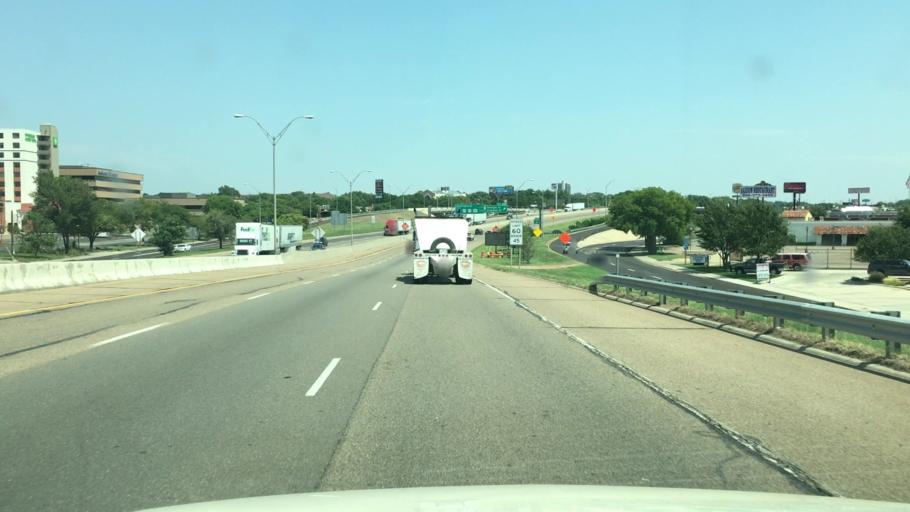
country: US
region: Texas
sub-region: Potter County
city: Amarillo
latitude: 35.1935
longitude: -101.8721
